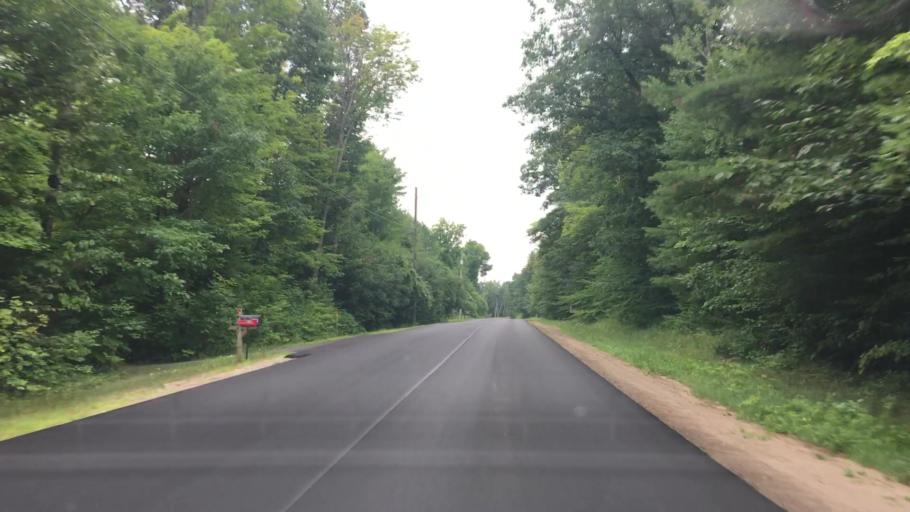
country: US
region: New York
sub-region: Clinton County
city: Peru
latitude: 44.5558
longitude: -73.5661
